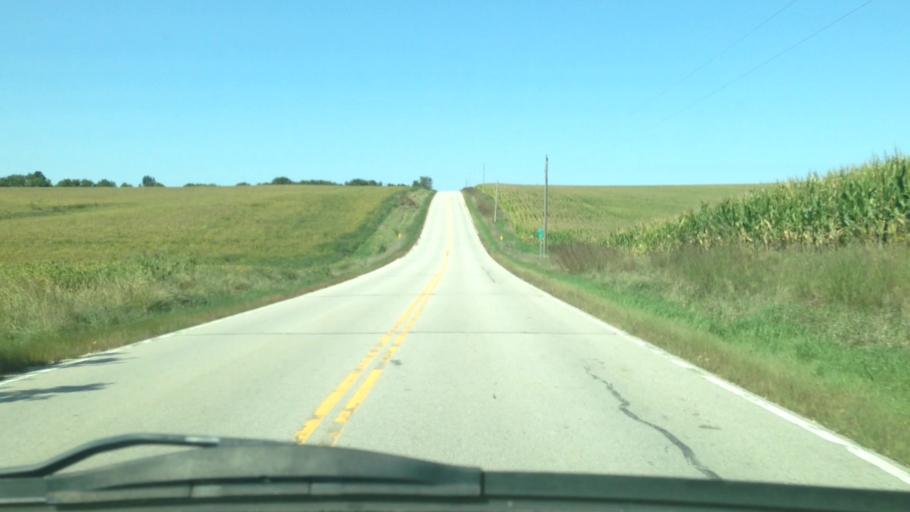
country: US
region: Minnesota
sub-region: Fillmore County
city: Rushford
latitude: 43.7096
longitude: -91.7703
